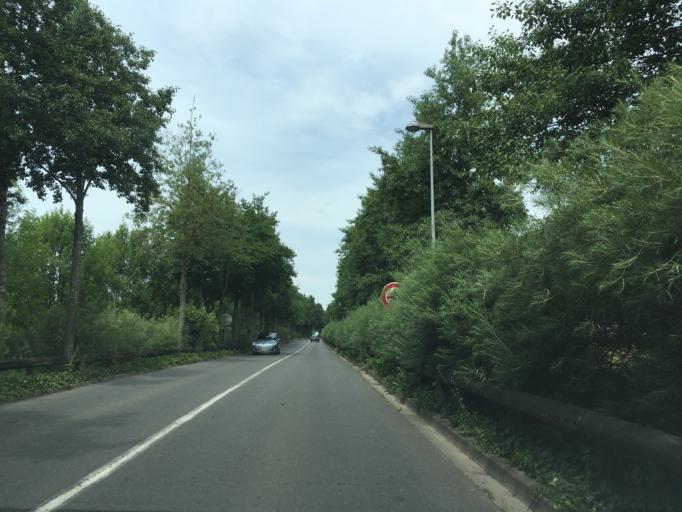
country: FR
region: Poitou-Charentes
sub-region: Departement des Deux-Sevres
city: Niort
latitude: 46.3294
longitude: -0.4891
